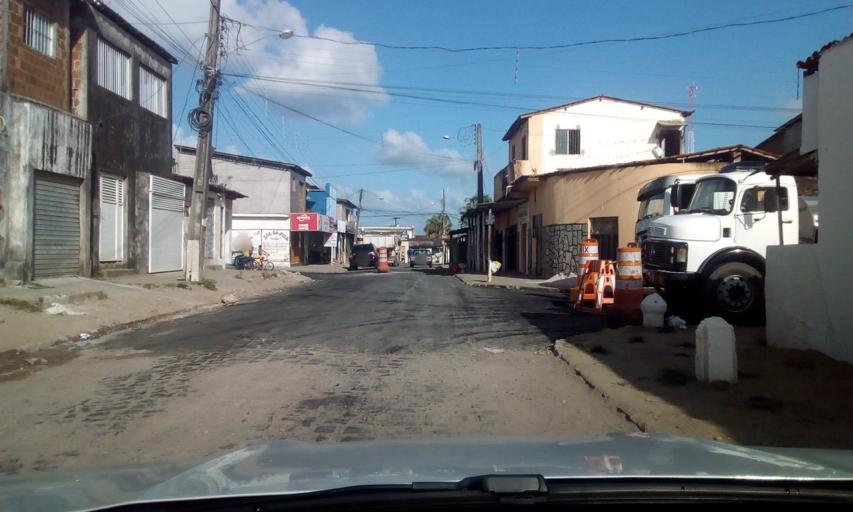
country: BR
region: Paraiba
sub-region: Conde
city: Conde
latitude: -7.1877
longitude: -34.8842
